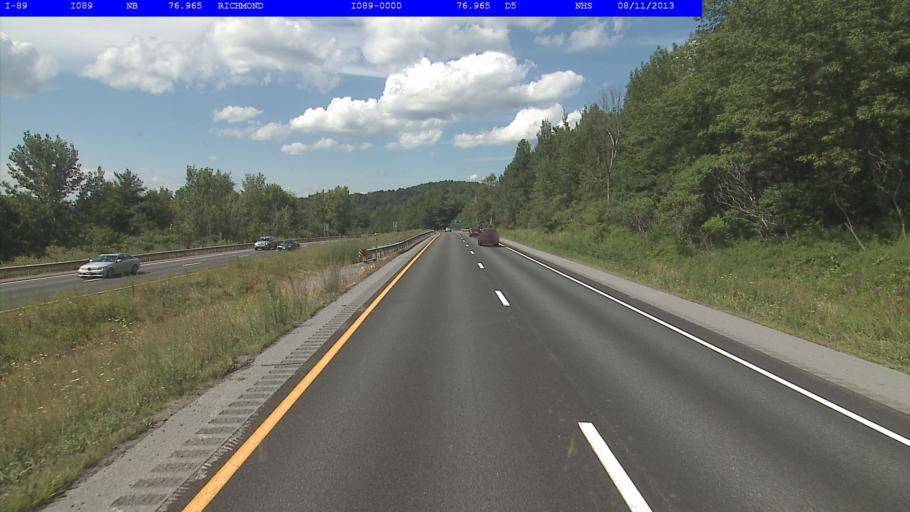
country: US
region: Vermont
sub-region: Chittenden County
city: Williston
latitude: 44.4101
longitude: -72.9906
